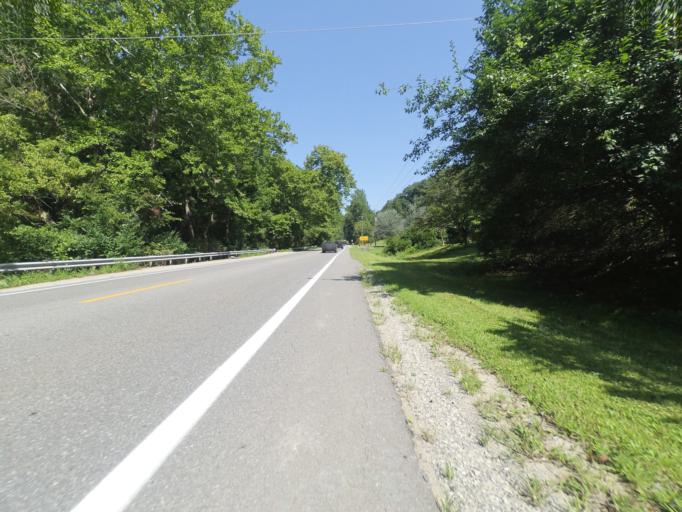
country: US
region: West Virginia
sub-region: Cabell County
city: Huntington
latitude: 38.3792
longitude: -82.4557
